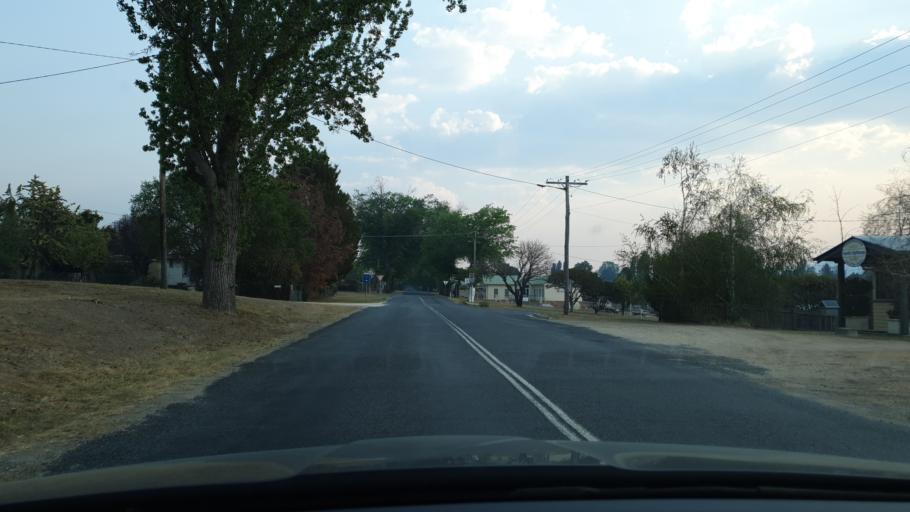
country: AU
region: New South Wales
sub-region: Tenterfield Municipality
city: Carrolls Creek
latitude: -29.0450
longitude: 152.0230
